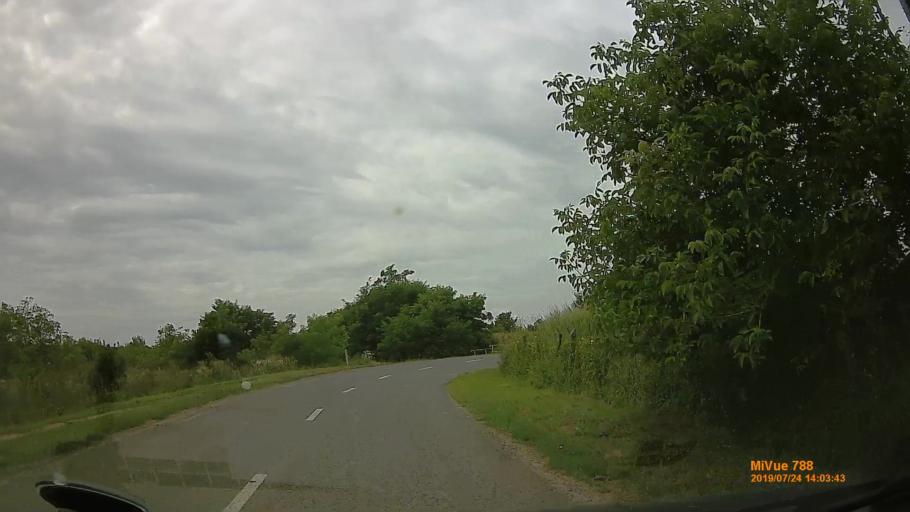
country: HU
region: Szabolcs-Szatmar-Bereg
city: Aranyosapati
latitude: 48.2807
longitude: 22.2834
